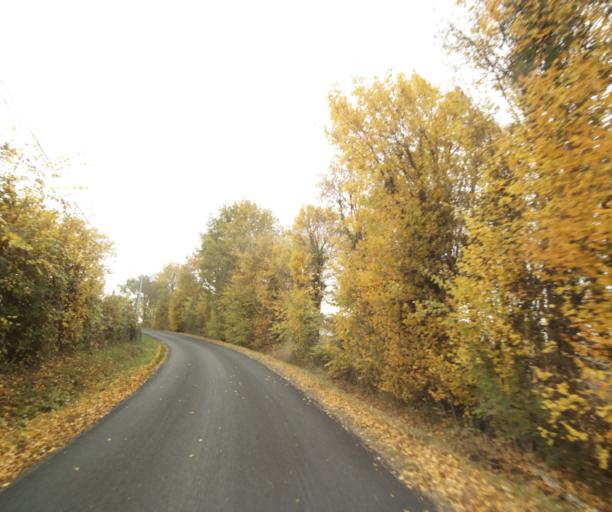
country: FR
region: Poitou-Charentes
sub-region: Departement de la Charente-Maritime
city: Saint-Georges-des-Coteaux
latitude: 45.7794
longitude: -0.6809
